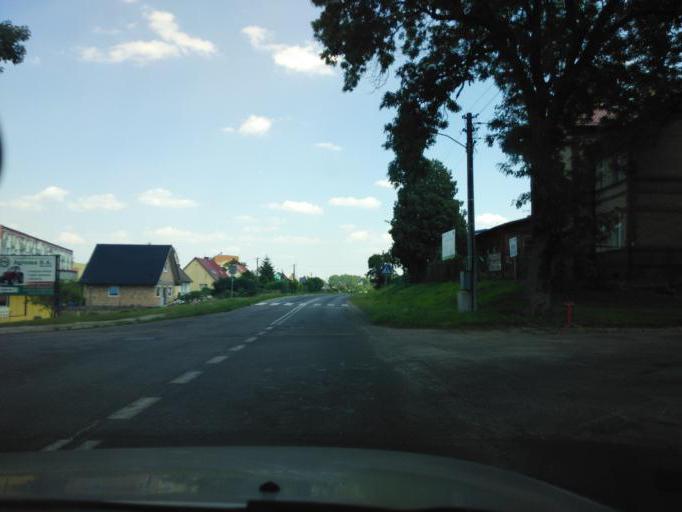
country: PL
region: West Pomeranian Voivodeship
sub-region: Powiat pyrzycki
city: Pyrzyce
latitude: 53.1370
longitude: 14.9076
